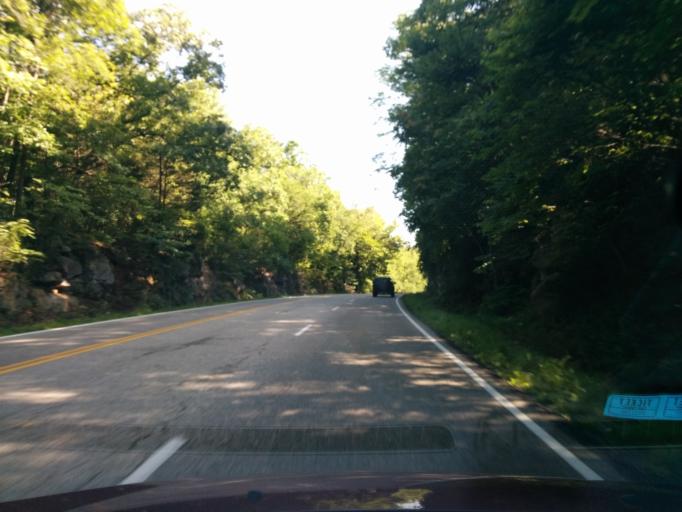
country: US
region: Virginia
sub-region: City of Lexington
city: Lexington
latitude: 37.7239
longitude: -79.4698
